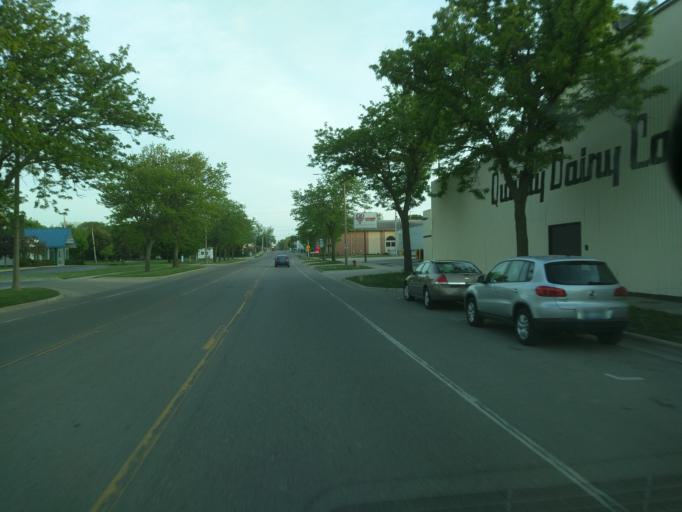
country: US
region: Michigan
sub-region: Ingham County
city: Lansing
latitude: 42.7180
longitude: -84.5524
